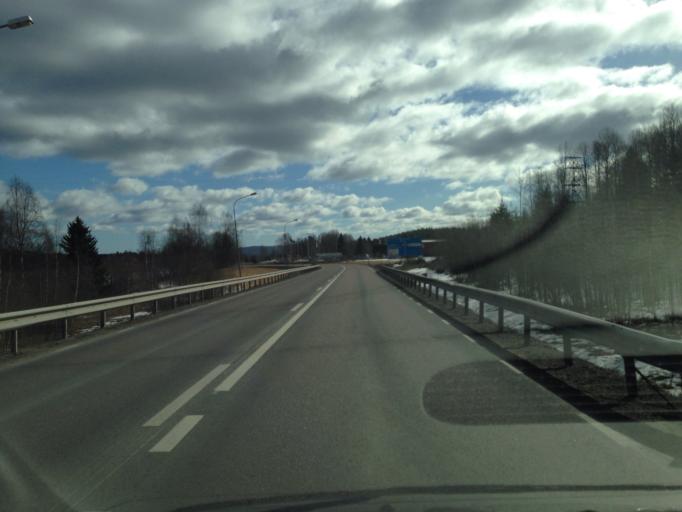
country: SE
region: Gaevleborg
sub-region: Ljusdals Kommun
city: Ljusdal
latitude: 61.8223
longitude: 16.0540
